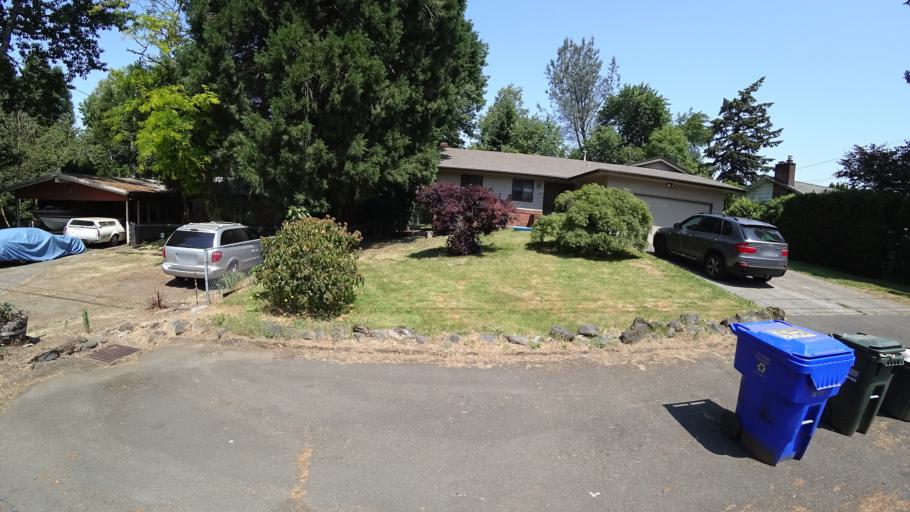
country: US
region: Oregon
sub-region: Multnomah County
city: Lents
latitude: 45.4605
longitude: -122.5698
